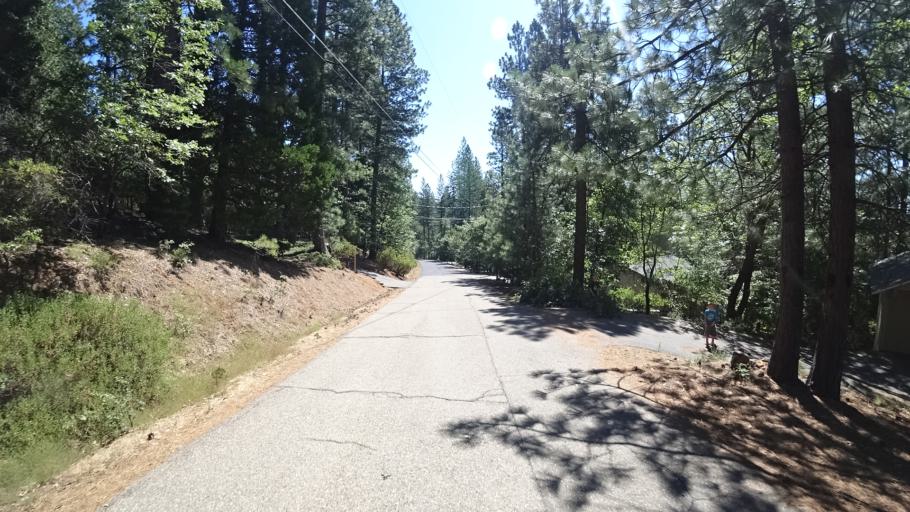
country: US
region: California
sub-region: Calaveras County
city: Arnold
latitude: 38.2389
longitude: -120.3732
